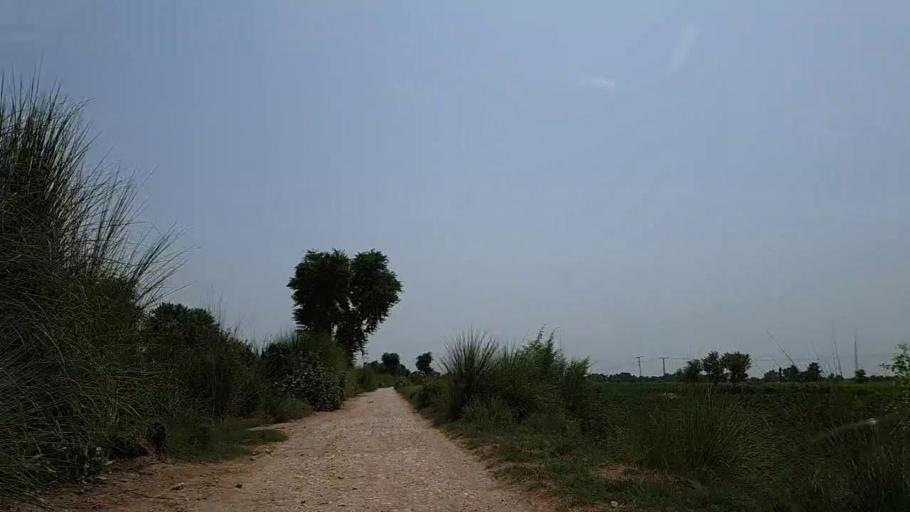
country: PK
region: Sindh
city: Adilpur
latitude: 27.9378
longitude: 69.3949
